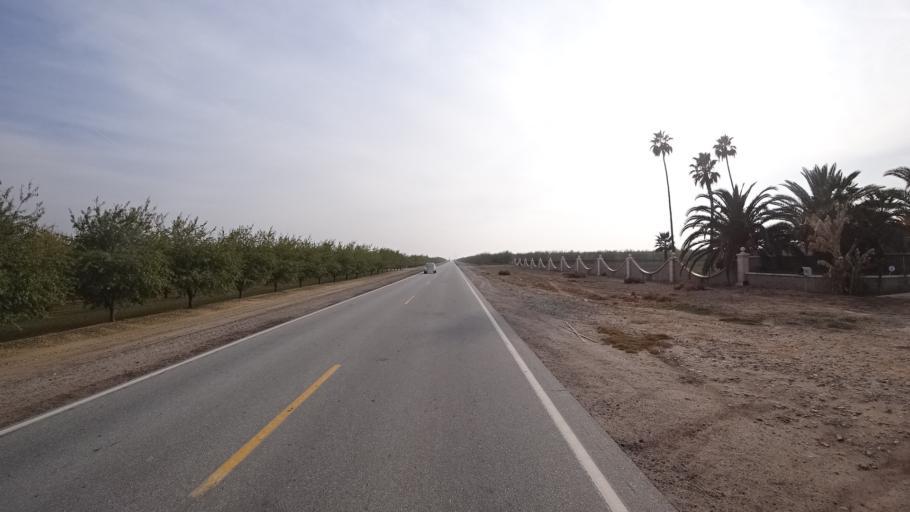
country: US
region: California
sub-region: Kern County
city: Greenacres
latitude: 35.2790
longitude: -119.1283
